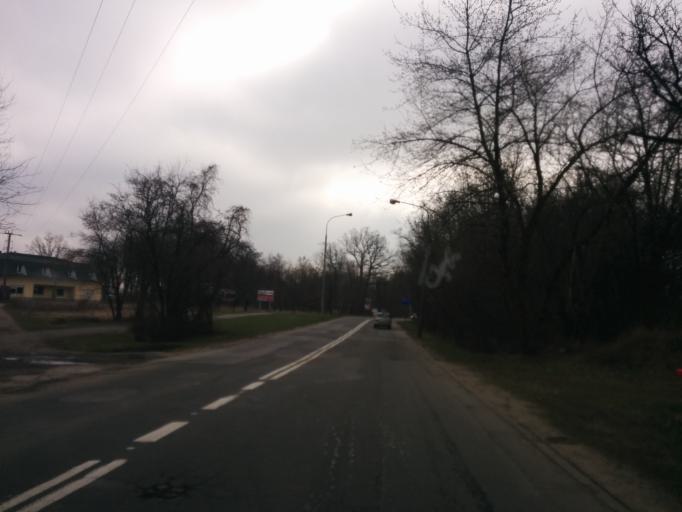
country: PL
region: Masovian Voivodeship
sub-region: Warszawa
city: Bialoleka
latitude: 52.3292
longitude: 20.9892
